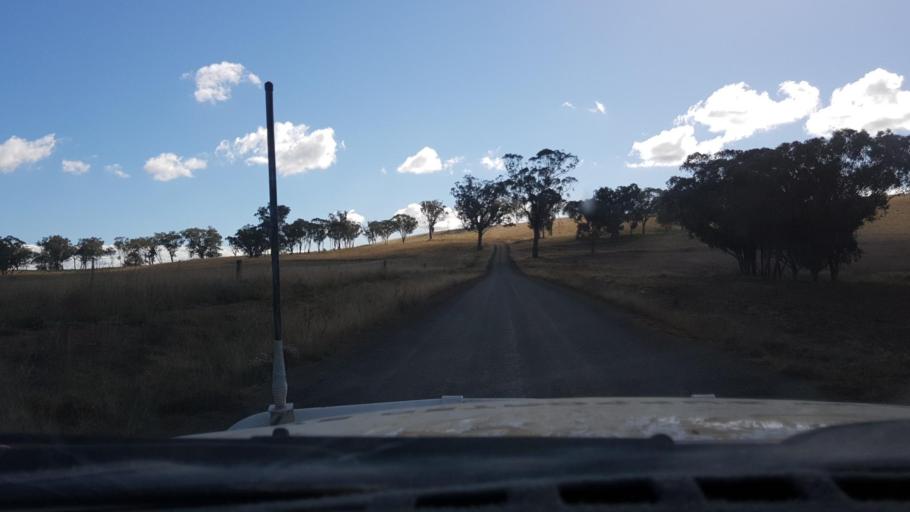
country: AU
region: New South Wales
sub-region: Narrabri
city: Blair Athol
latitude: -30.5535
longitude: 150.4616
